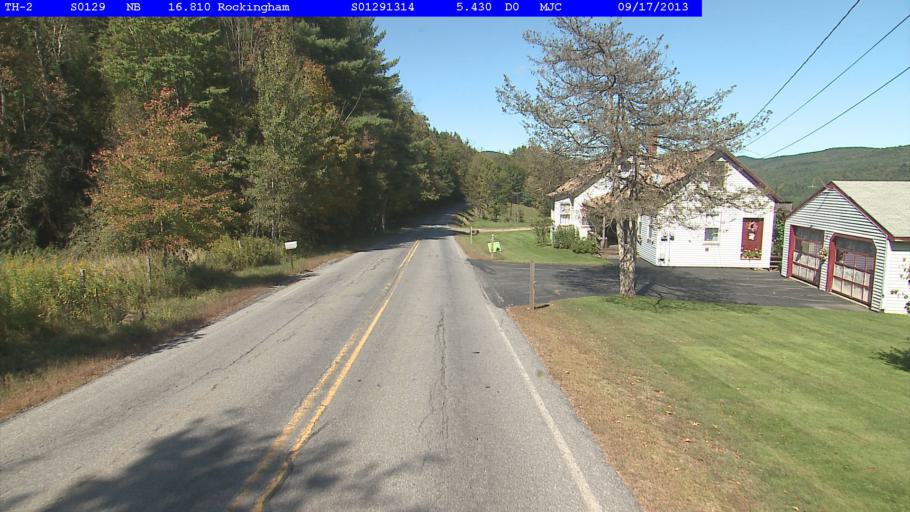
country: US
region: Vermont
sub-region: Windham County
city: Rockingham
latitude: 43.1946
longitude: -72.5115
